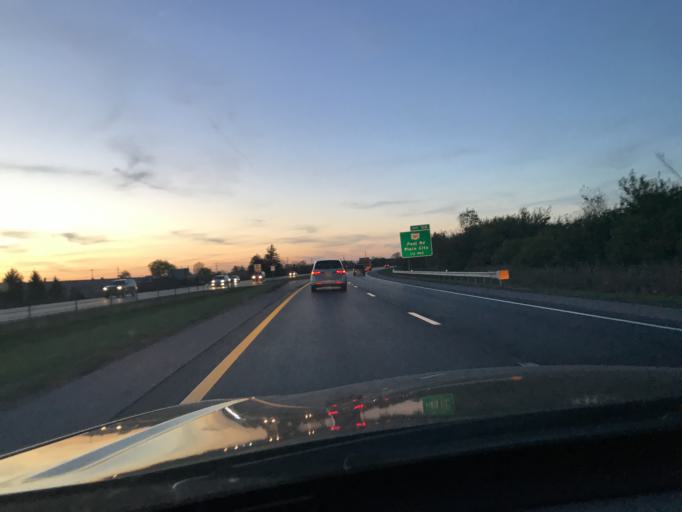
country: US
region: Ohio
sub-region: Franklin County
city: Dublin
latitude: 40.1005
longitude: -83.1713
